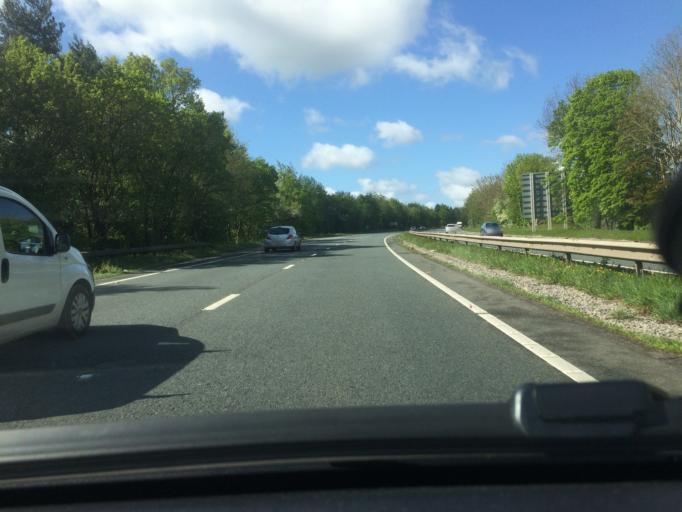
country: GB
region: Wales
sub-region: Wrexham
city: Wrexham
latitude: 53.0501
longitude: -3.0159
